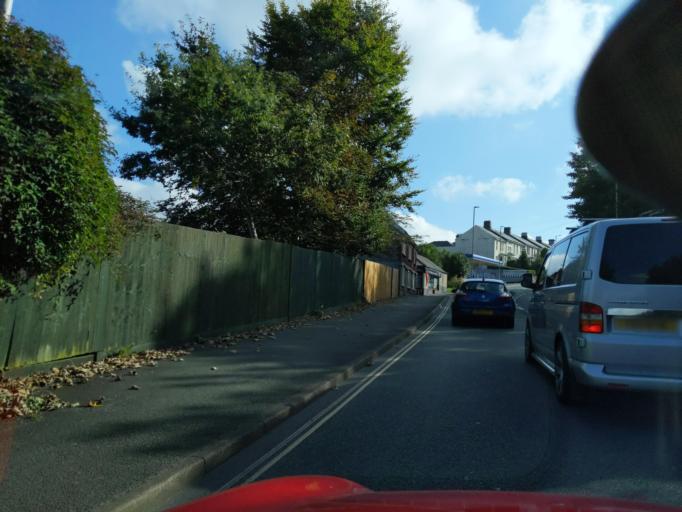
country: GB
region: England
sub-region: Plymouth
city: Plymouth
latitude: 50.3979
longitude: -4.1344
